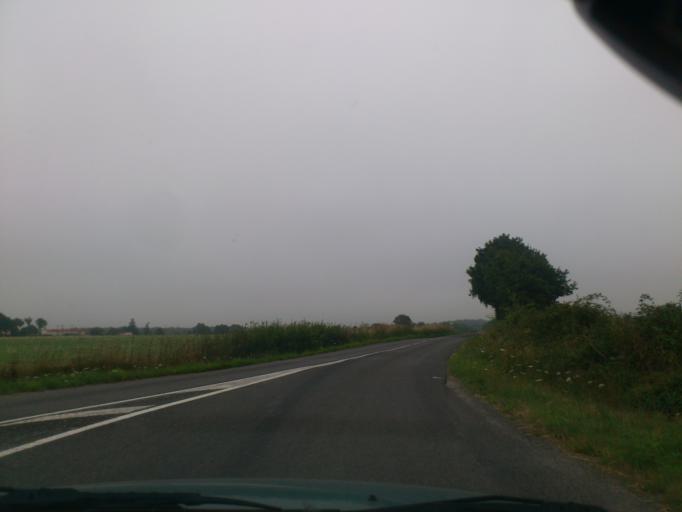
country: FR
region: Pays de la Loire
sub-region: Departement de la Vendee
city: Saint-Hilaire-de-Loulay
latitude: 46.9968
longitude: -1.3796
